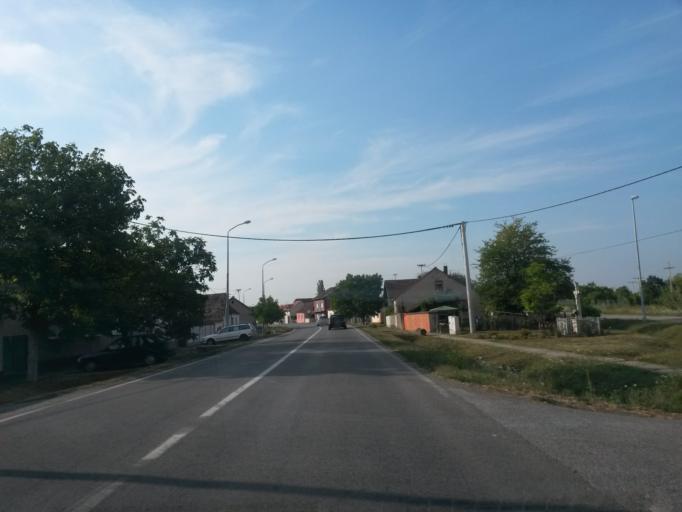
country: HR
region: Brodsko-Posavska
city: Vrpolje
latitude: 45.2063
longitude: 18.4091
